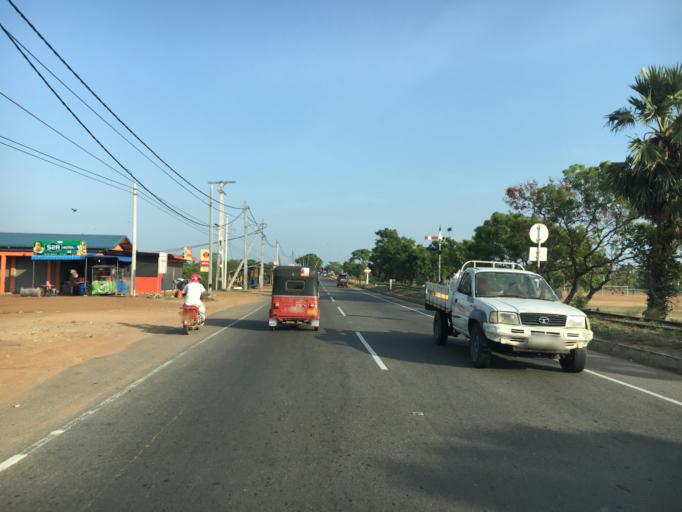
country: LK
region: Eastern Province
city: Eravur Town
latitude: 7.9180
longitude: 81.5186
